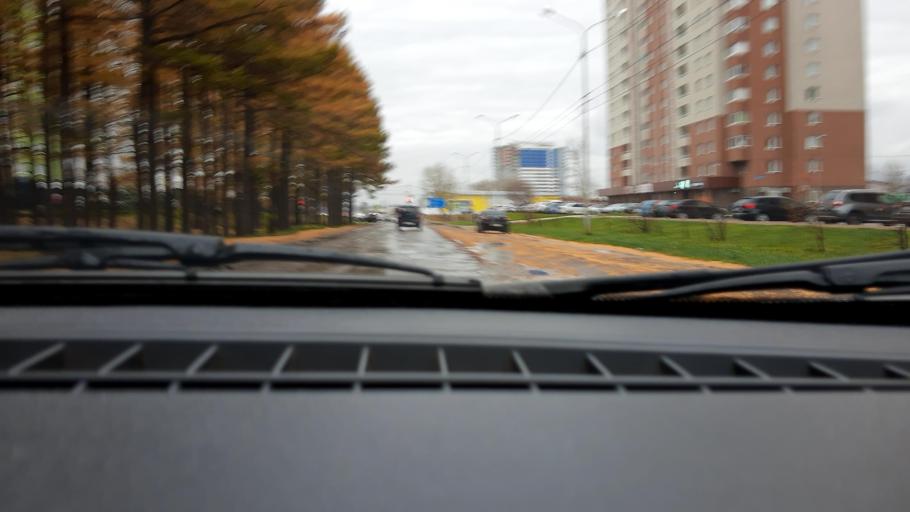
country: RU
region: Bashkortostan
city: Mikhaylovka
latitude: 54.7942
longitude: 55.8689
